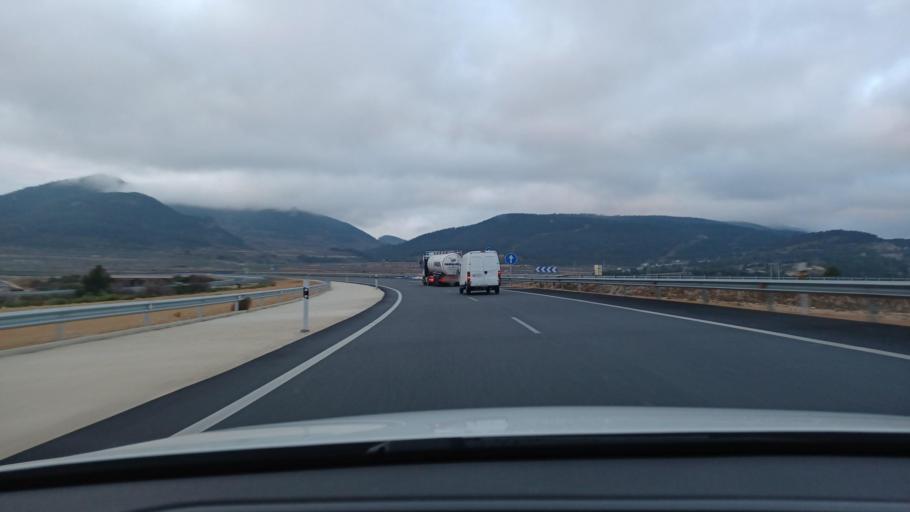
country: ES
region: Valencia
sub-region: Provincia de Valencia
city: La Font de la Figuera
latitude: 38.8298
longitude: -0.8911
